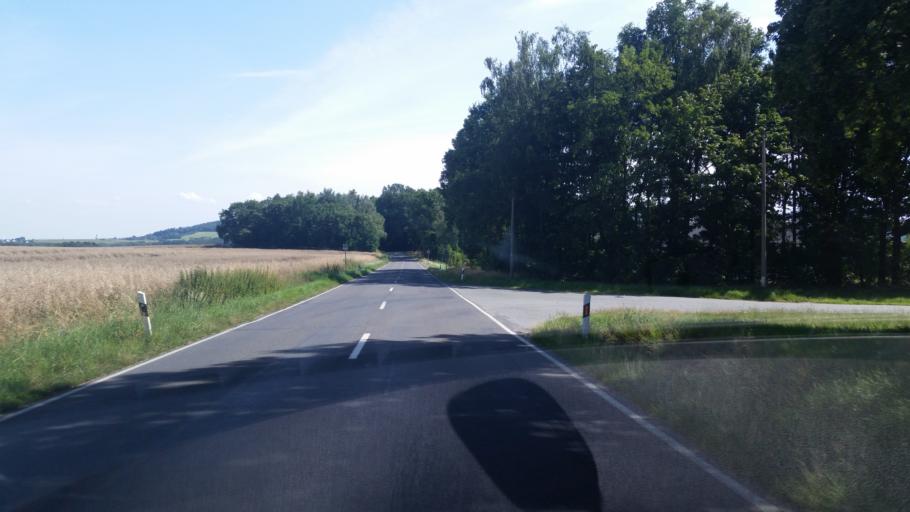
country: DE
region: Saxony
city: Kamenz
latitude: 51.2982
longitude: 14.0512
